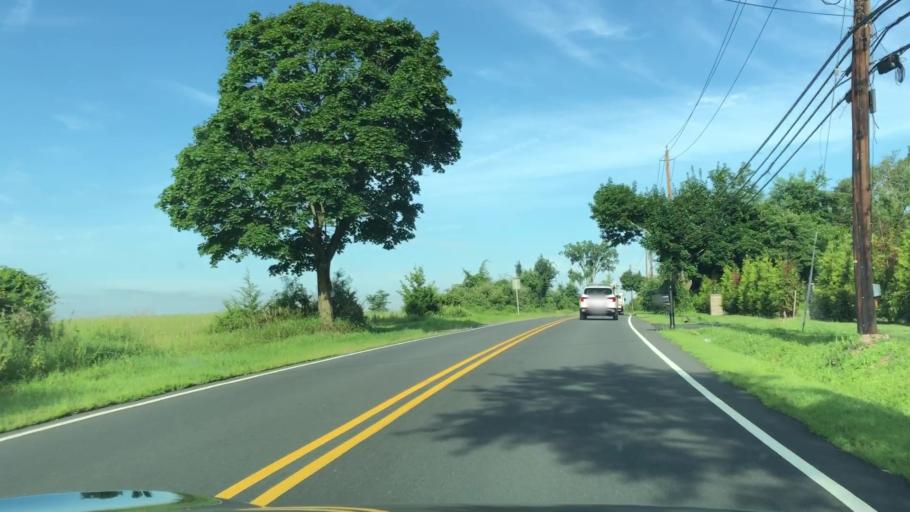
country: US
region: New Jersey
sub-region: Mercer County
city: Pennington
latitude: 40.3380
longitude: -74.7639
